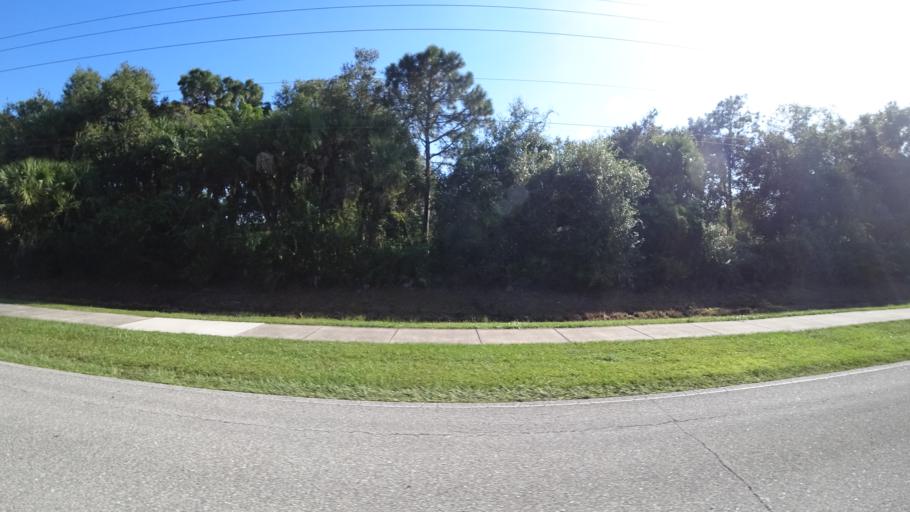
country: US
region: Florida
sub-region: Sarasota County
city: Desoto Lakes
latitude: 27.4325
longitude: -82.4753
